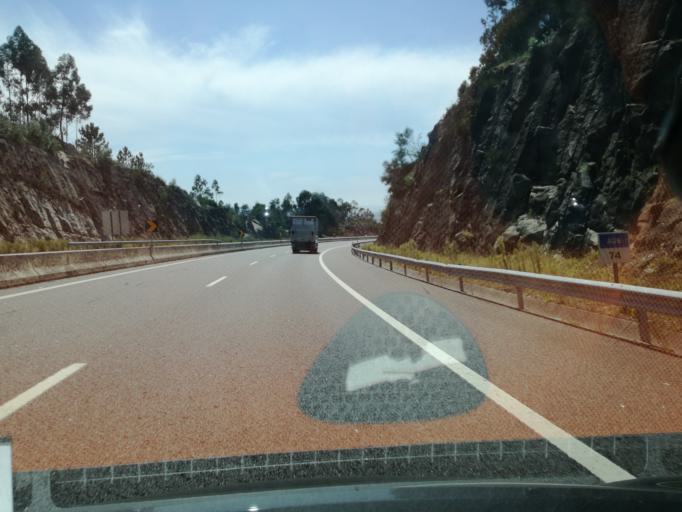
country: PT
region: Viana do Castelo
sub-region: Viana do Castelo
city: Meadela
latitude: 41.7403
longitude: -8.7920
